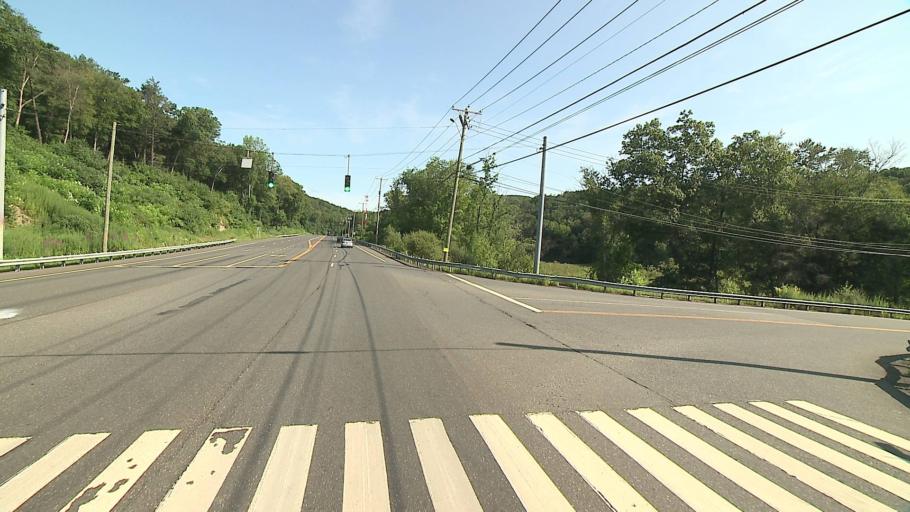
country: US
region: Connecticut
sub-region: Fairfield County
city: Danbury
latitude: 41.3467
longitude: -73.4688
